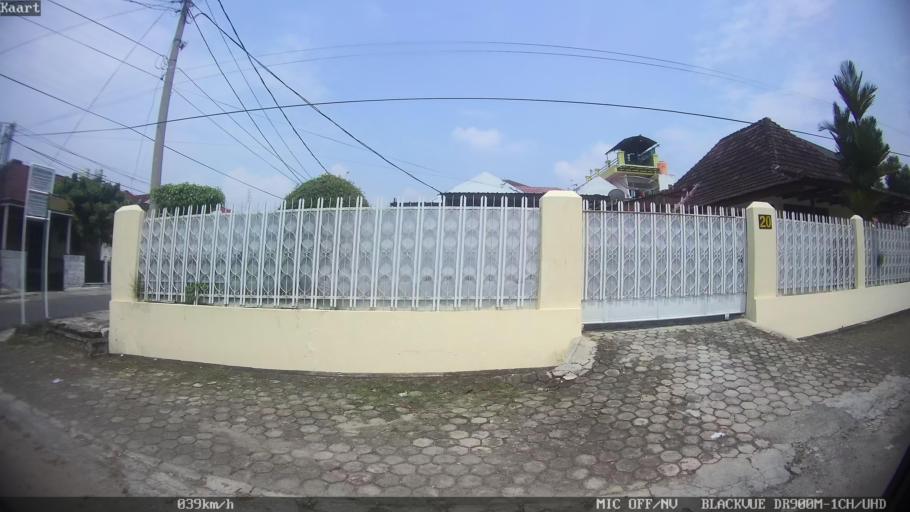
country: ID
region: Lampung
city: Bandarlampung
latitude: -5.4268
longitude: 105.2718
